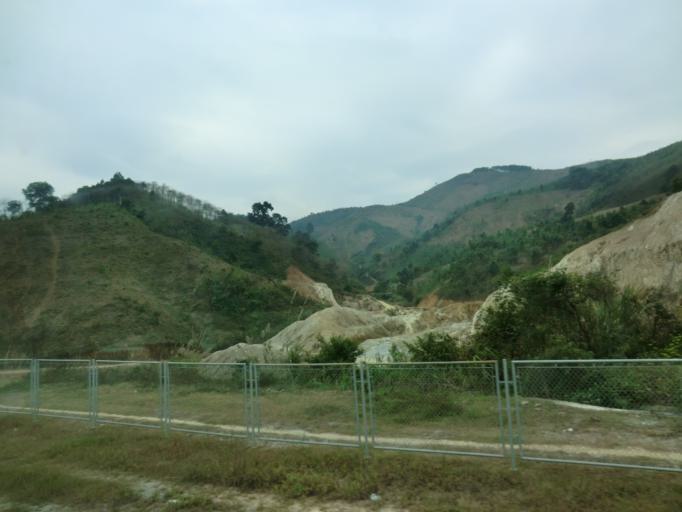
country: VN
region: Yen Bai
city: Thi Tran Yen The
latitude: 21.9355
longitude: 104.5918
